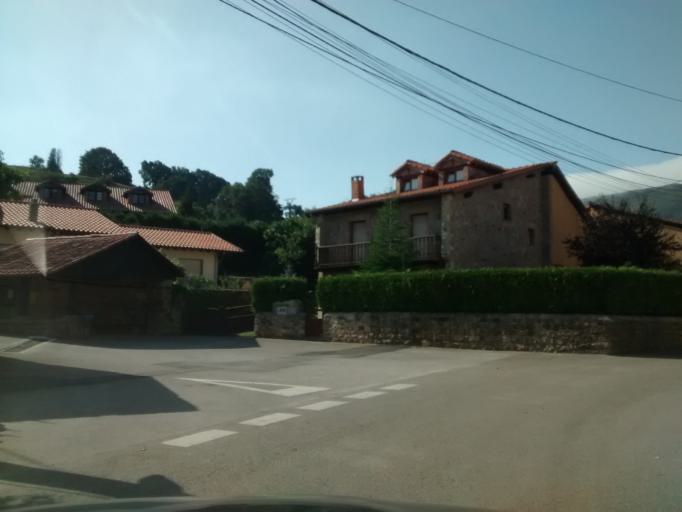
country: ES
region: Cantabria
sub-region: Provincia de Cantabria
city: Ruente
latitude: 43.2583
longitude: -4.2465
